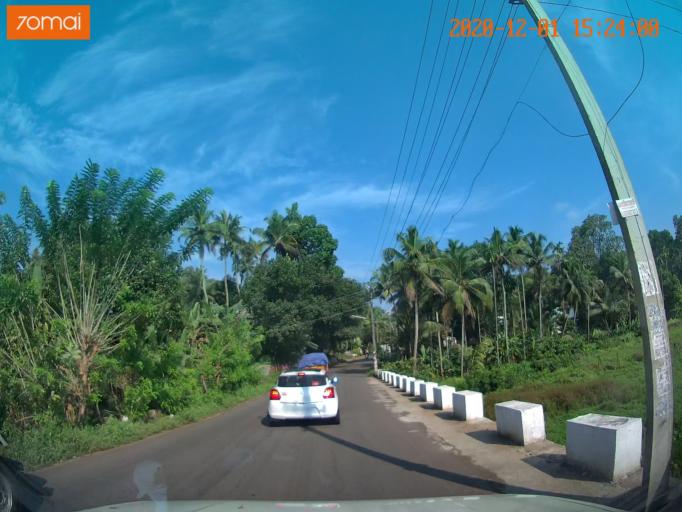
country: IN
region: Kerala
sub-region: Ernakulam
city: Muvattupuzha
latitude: 9.9527
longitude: 76.5527
